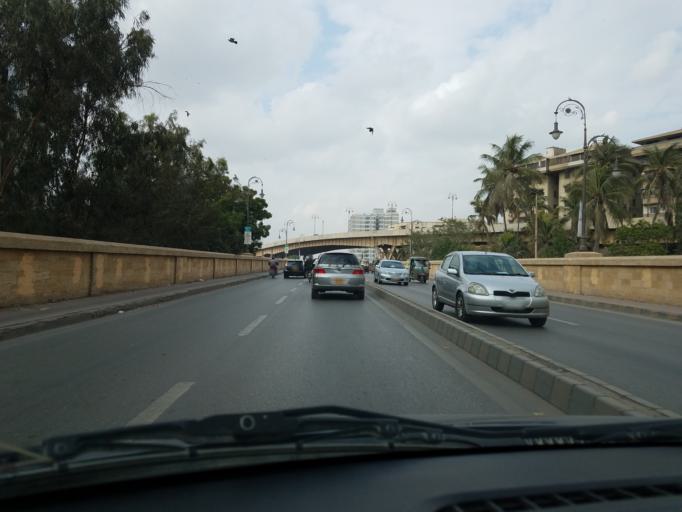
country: PK
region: Sindh
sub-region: Karachi District
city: Karachi
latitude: 24.8393
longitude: 67.0328
